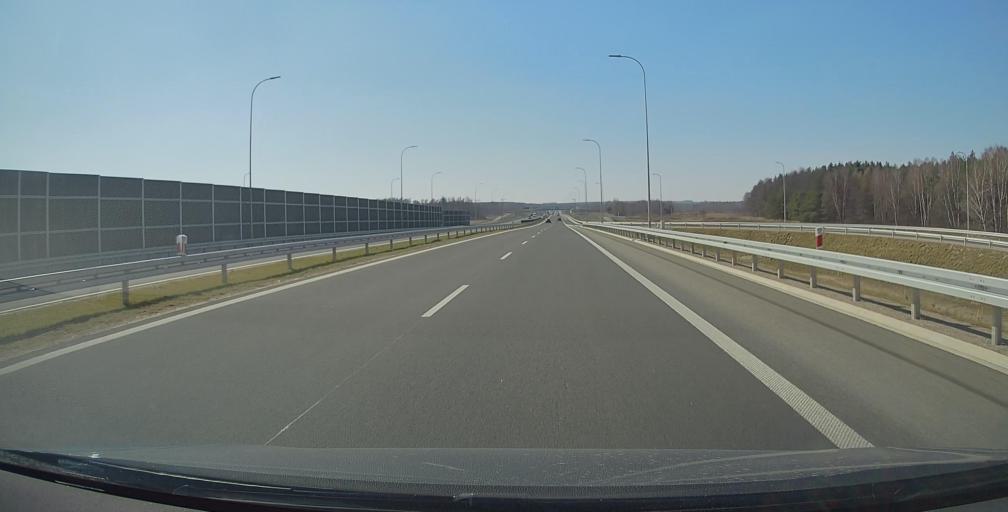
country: PL
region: Subcarpathian Voivodeship
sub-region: Powiat lezajski
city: Letownia
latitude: 50.3325
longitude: 22.1935
